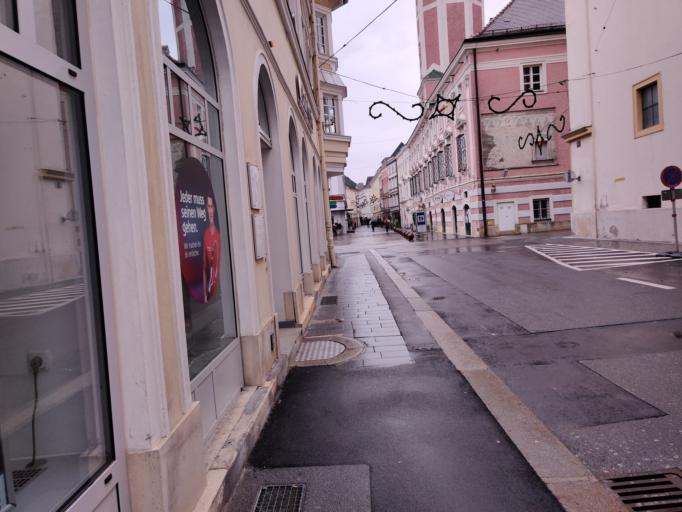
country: AT
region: Lower Austria
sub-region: Sankt Polten Stadt
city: Sankt Poelten
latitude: 48.2045
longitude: 15.6222
